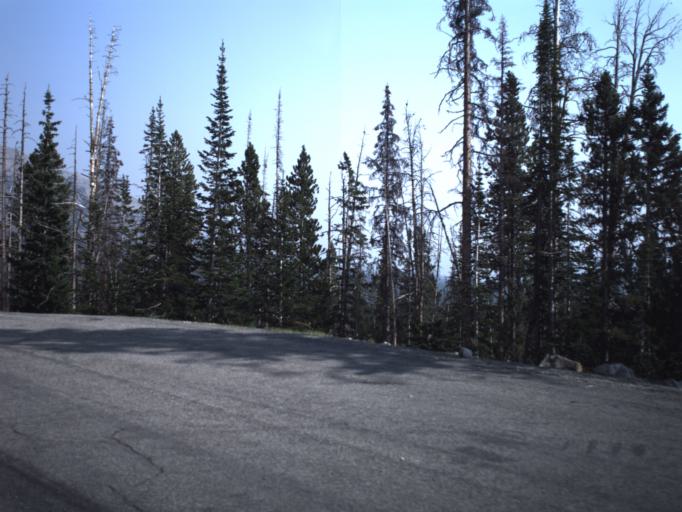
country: US
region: Utah
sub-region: Summit County
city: Kamas
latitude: 40.7193
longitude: -110.8699
